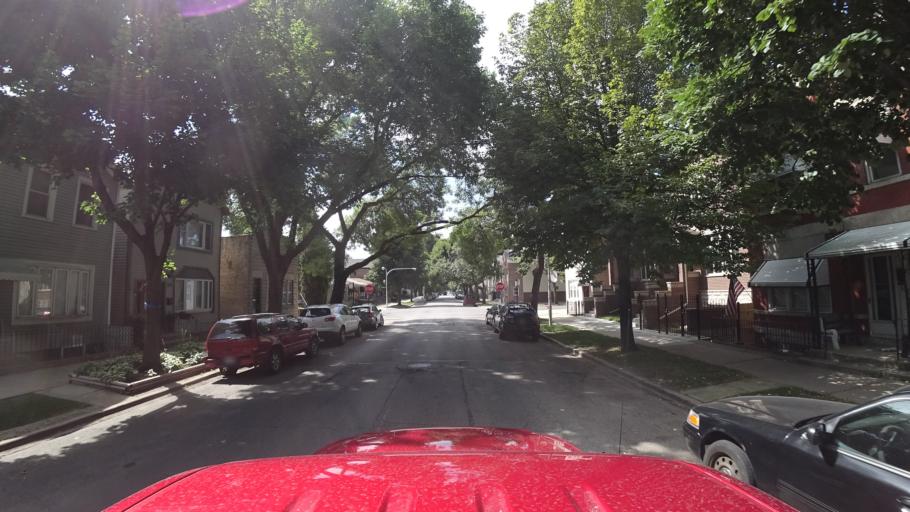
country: US
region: Illinois
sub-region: Cook County
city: Chicago
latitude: 41.8294
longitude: -87.6449
